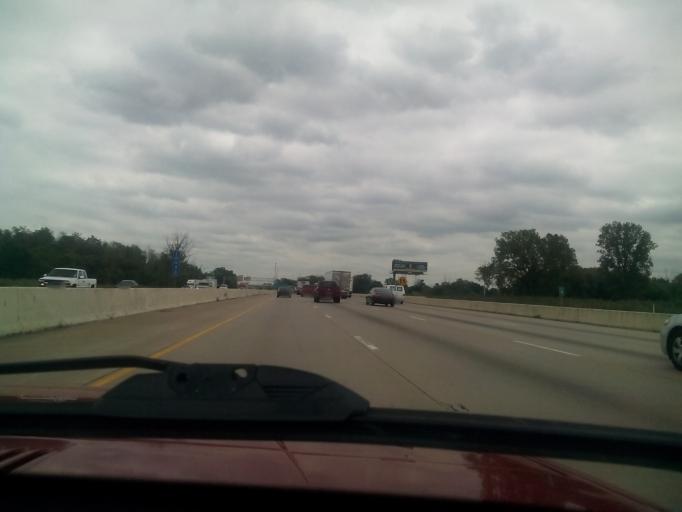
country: US
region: Indiana
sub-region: Lake County
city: Gary
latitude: 41.5687
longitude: -87.3546
